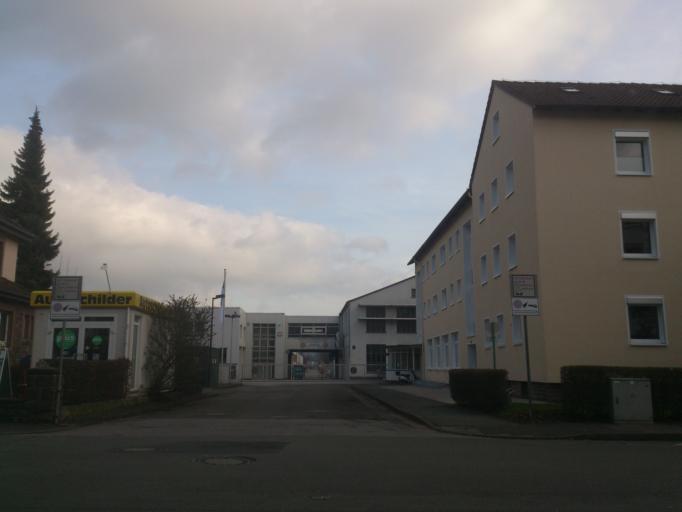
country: DE
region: North Rhine-Westphalia
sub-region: Regierungsbezirk Detmold
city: Hoexter
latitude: 51.7784
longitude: 9.3885
